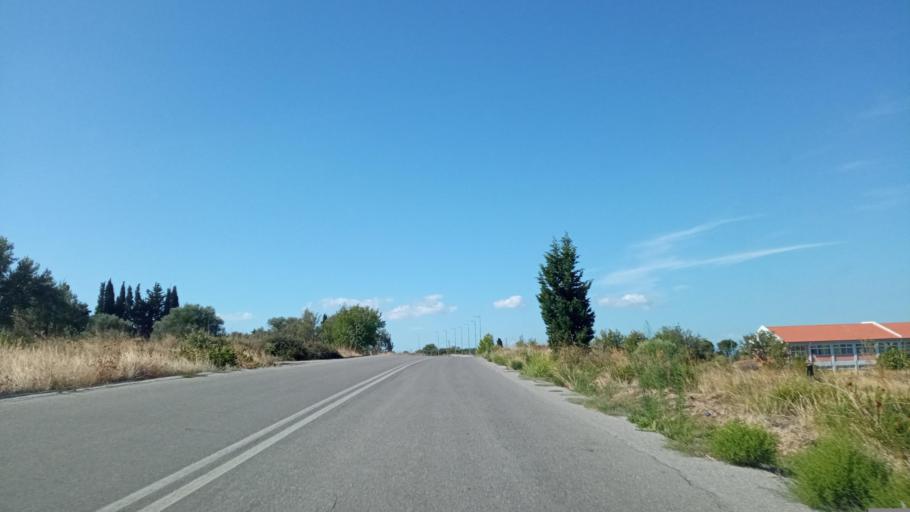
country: GR
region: Central Greece
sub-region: Nomos Evvoias
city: Psachna
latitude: 38.5850
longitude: 23.7720
